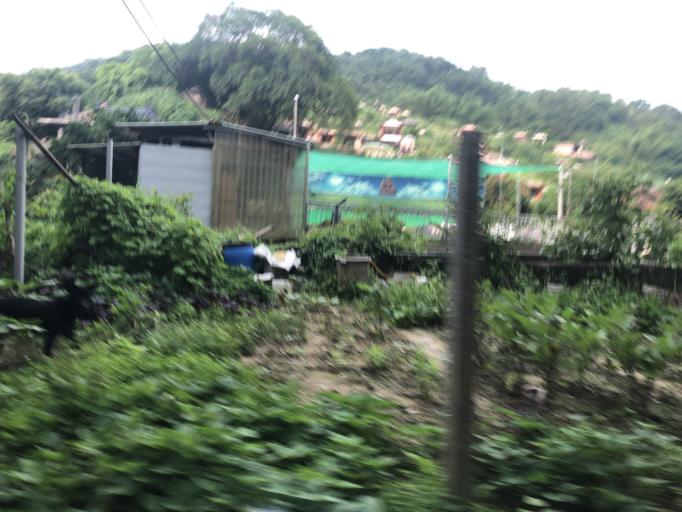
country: TW
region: Taiwan
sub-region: Taoyuan
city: Taoyuan
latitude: 24.9234
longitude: 121.3801
